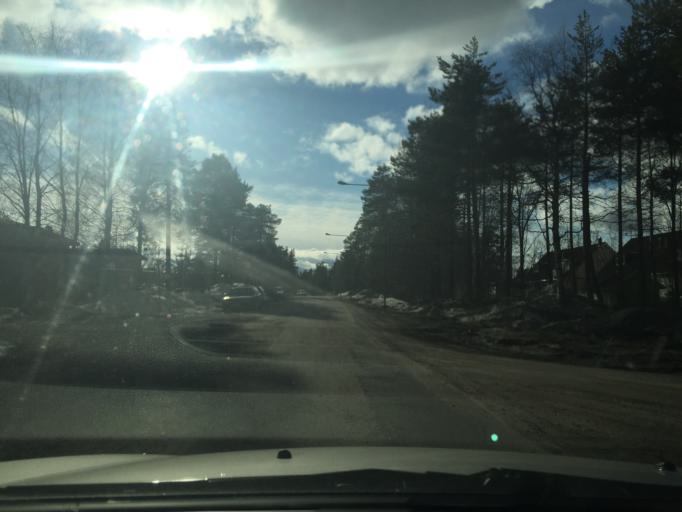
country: SE
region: Norrbotten
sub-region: Lulea Kommun
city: Lulea
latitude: 65.5947
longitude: 22.2405
